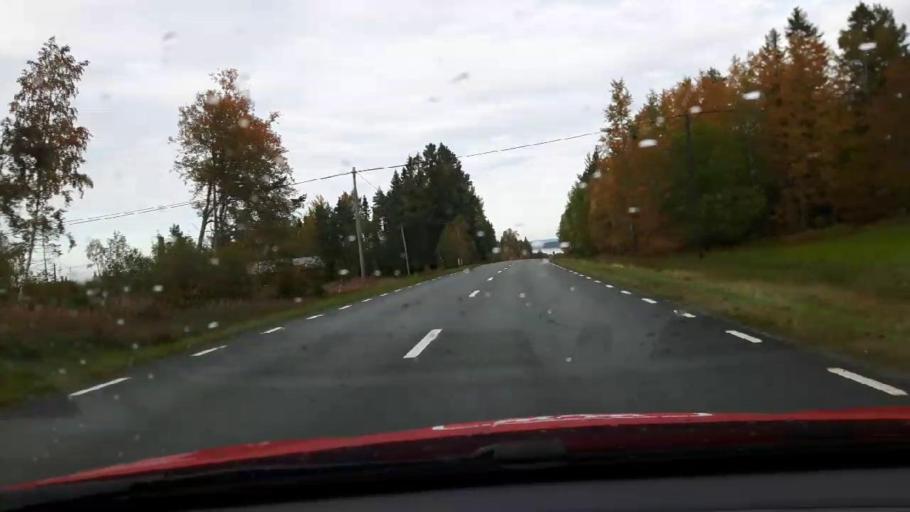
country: SE
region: Jaemtland
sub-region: Krokoms Kommun
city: Krokom
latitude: 63.1143
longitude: 14.2932
